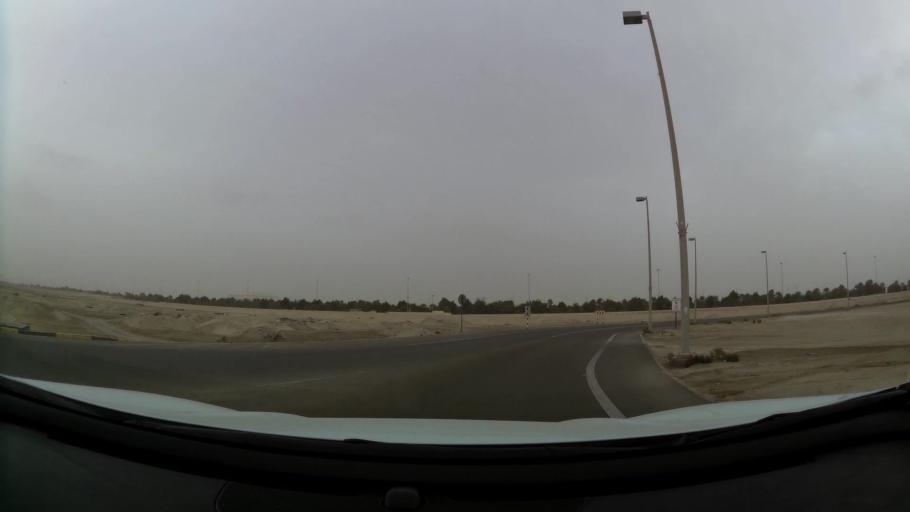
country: AE
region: Abu Dhabi
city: Abu Dhabi
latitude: 24.4264
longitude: 54.5449
